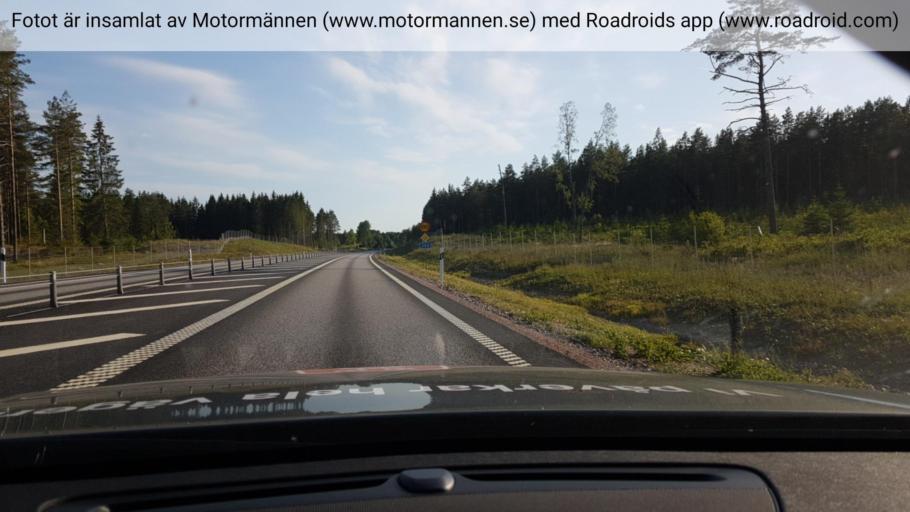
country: SE
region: Uppsala
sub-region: Osthammars Kommun
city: Gimo
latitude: 60.1231
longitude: 18.1481
